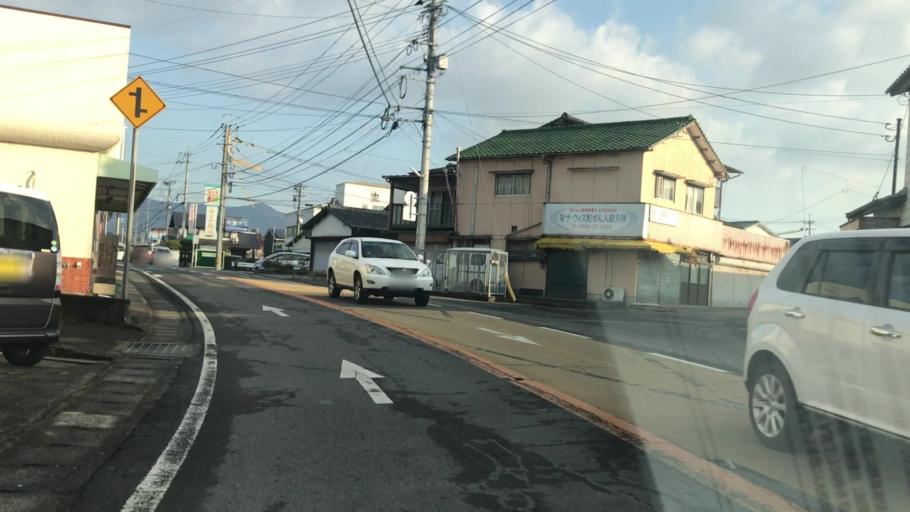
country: JP
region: Saga Prefecture
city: Takeocho-takeo
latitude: 33.2010
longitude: 130.0243
